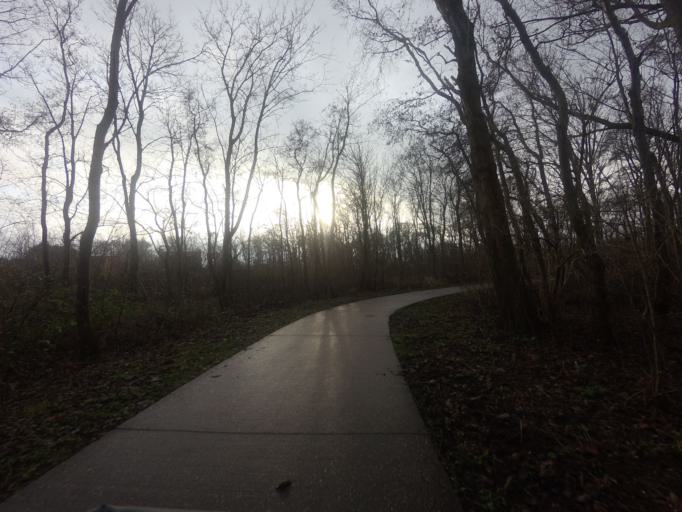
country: NL
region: North Holland
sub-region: Gemeente Texel
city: Den Burg
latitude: 53.1566
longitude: 4.8473
